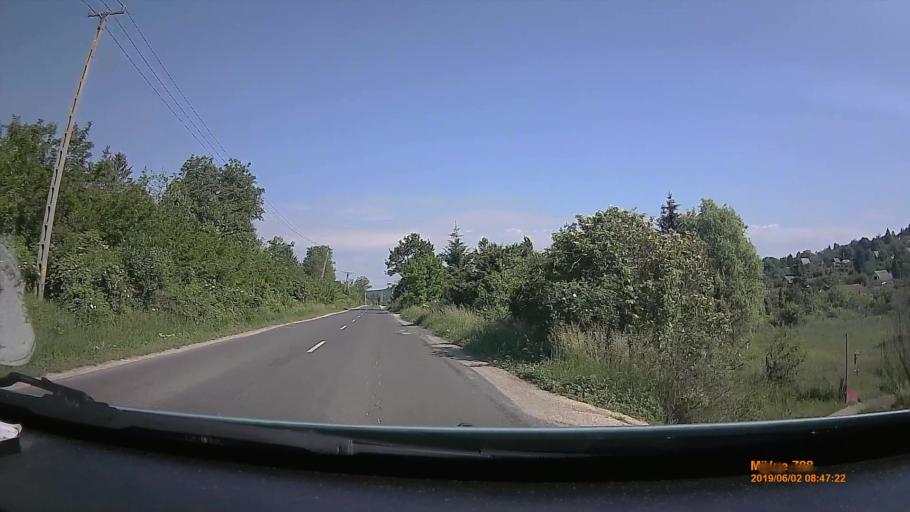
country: HU
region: Borsod-Abauj-Zemplen
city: Sajobabony
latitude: 48.1284
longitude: 20.7139
